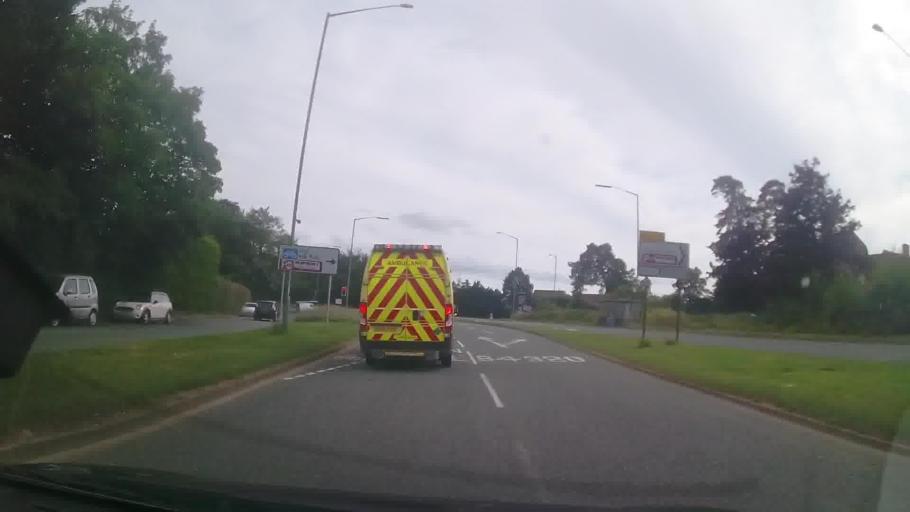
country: GB
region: England
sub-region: Shropshire
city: Bicton
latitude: 52.7149
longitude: -2.7928
